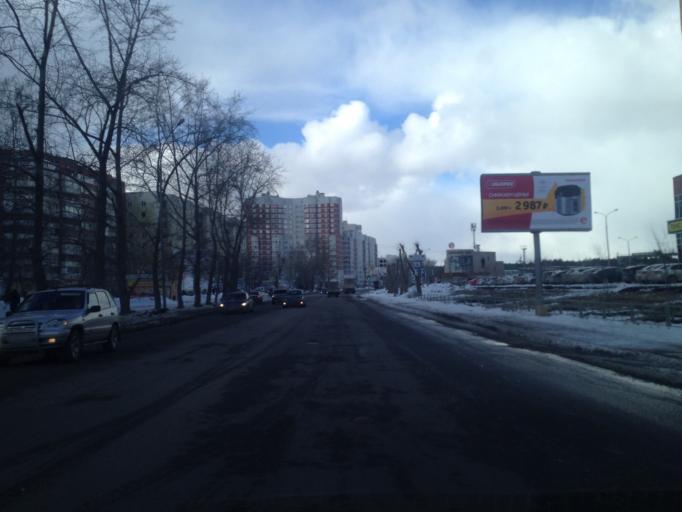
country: RU
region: Sverdlovsk
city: Yekaterinburg
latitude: 56.9066
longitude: 60.6212
